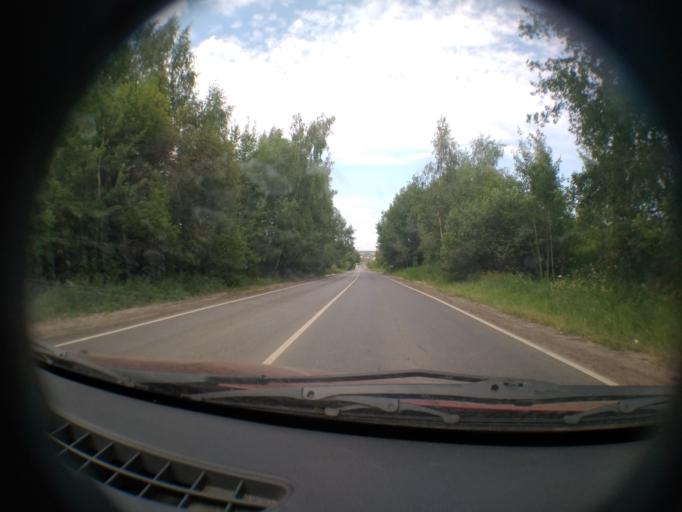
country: RU
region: Moskovskaya
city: Ostrovtsy
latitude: 55.5269
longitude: 38.0016
